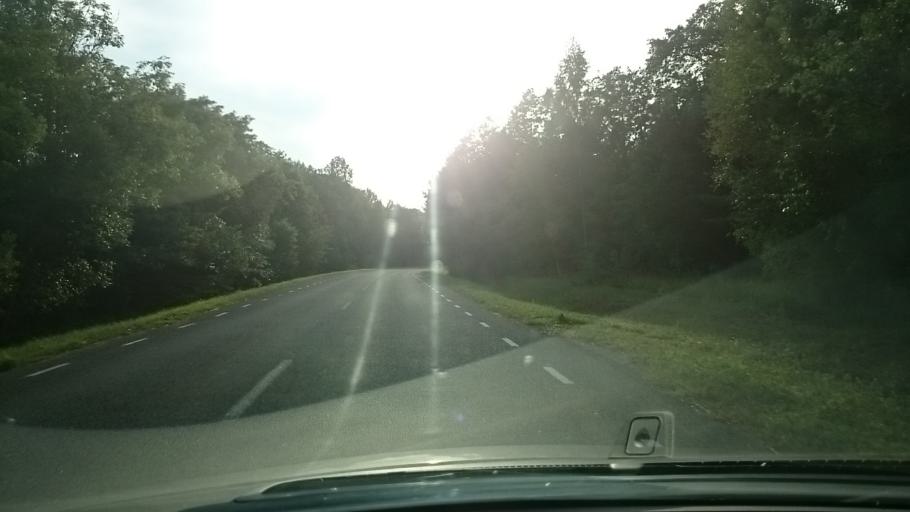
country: EE
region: Saare
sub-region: Kuressaare linn
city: Kuressaare
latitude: 58.4064
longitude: 22.2885
